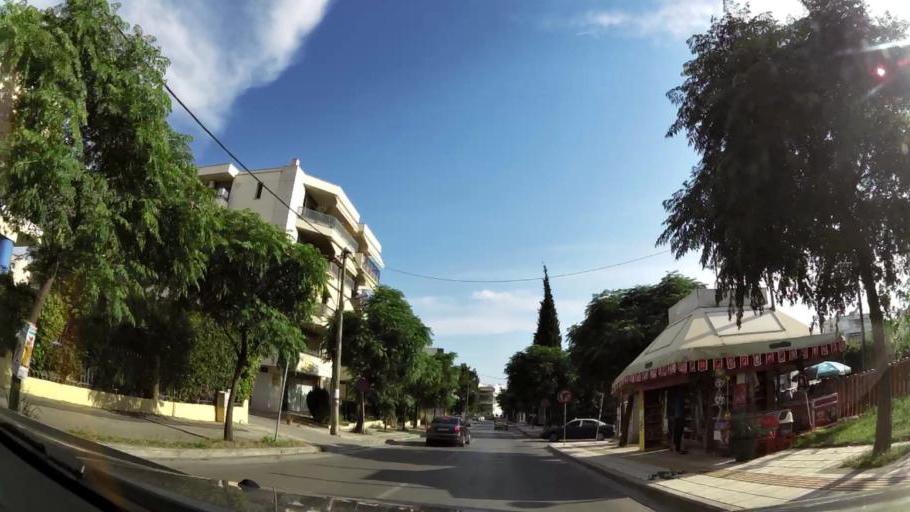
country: GR
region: Central Macedonia
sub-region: Nomos Thessalonikis
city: Kalamaria
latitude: 40.5756
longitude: 22.9633
